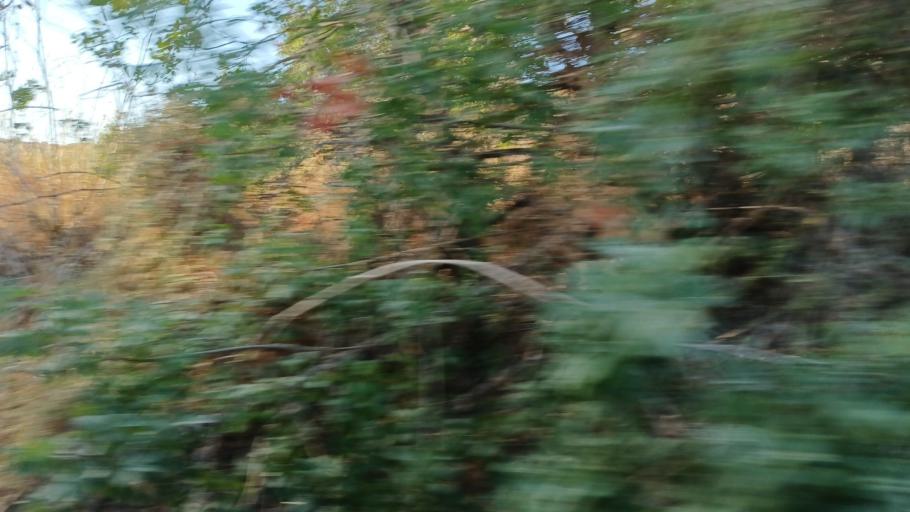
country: CY
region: Pafos
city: Polis
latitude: 34.9516
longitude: 32.4731
